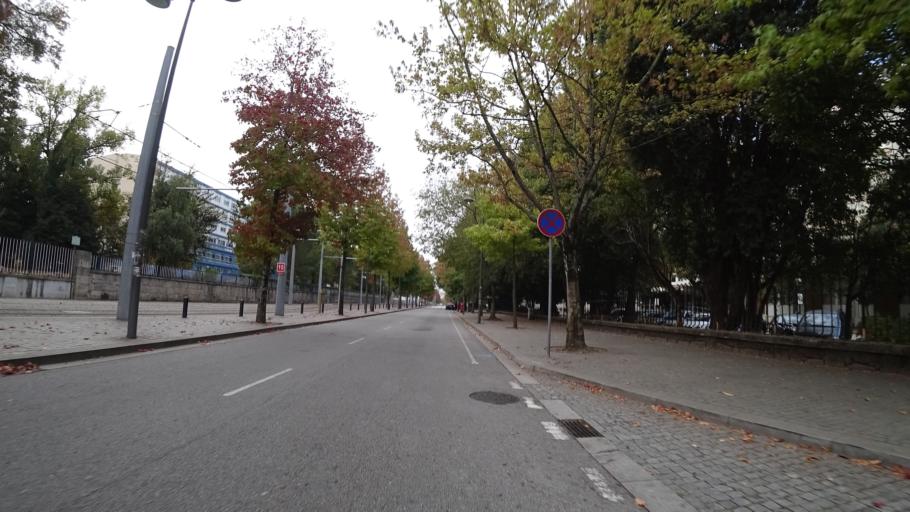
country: PT
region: Porto
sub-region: Matosinhos
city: Sao Mamede de Infesta
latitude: 41.1833
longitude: -8.6037
